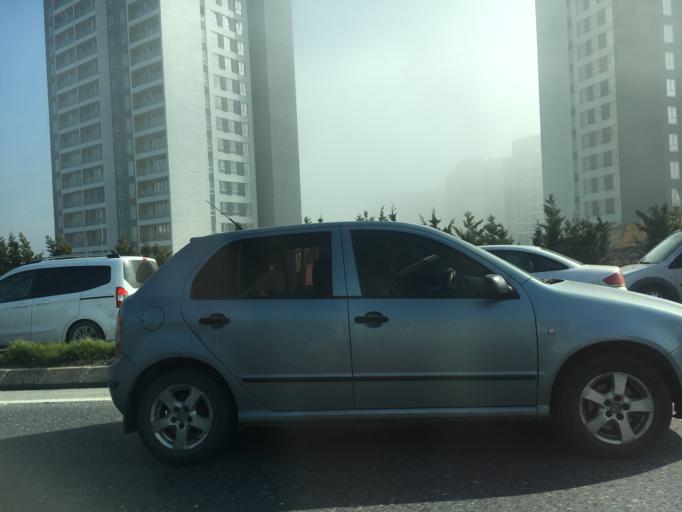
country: TR
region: Istanbul
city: Esenyurt
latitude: 41.0535
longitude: 28.6843
